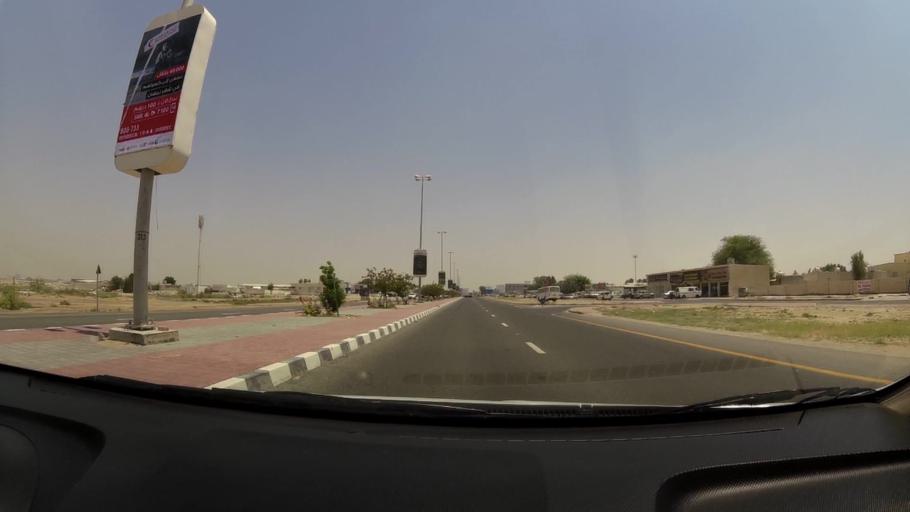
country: AE
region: Umm al Qaywayn
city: Umm al Qaywayn
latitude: 25.5133
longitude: 55.5455
